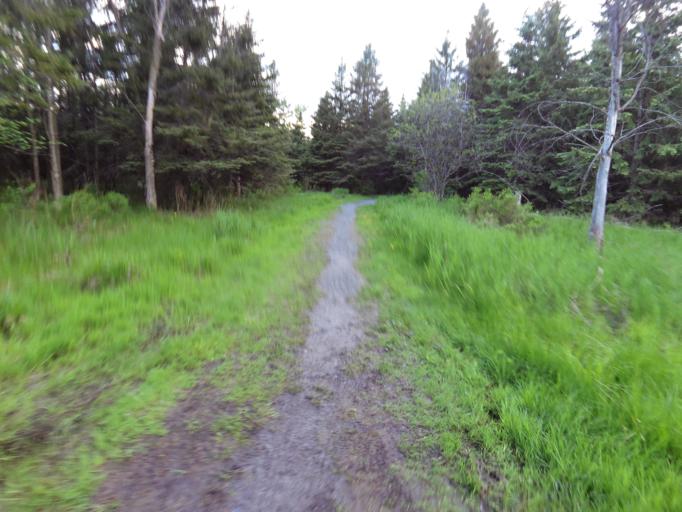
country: CA
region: Ontario
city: Bells Corners
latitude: 45.3329
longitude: -75.8596
